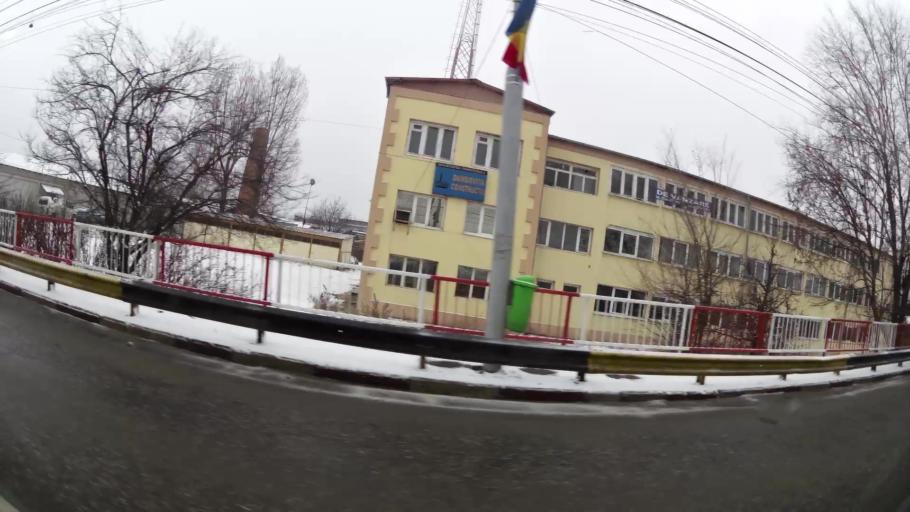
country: RO
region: Dambovita
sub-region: Municipiul Targoviste
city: Targoviste
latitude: 44.9150
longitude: 25.4512
